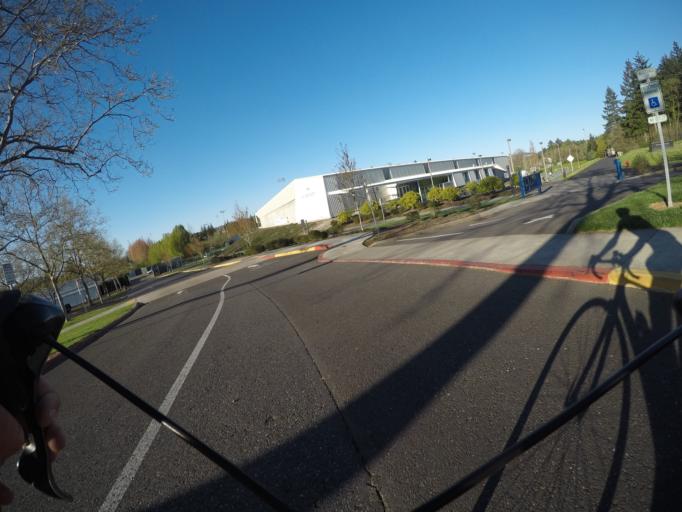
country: US
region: Oregon
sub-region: Washington County
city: Oak Hills
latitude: 45.5198
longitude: -122.8379
